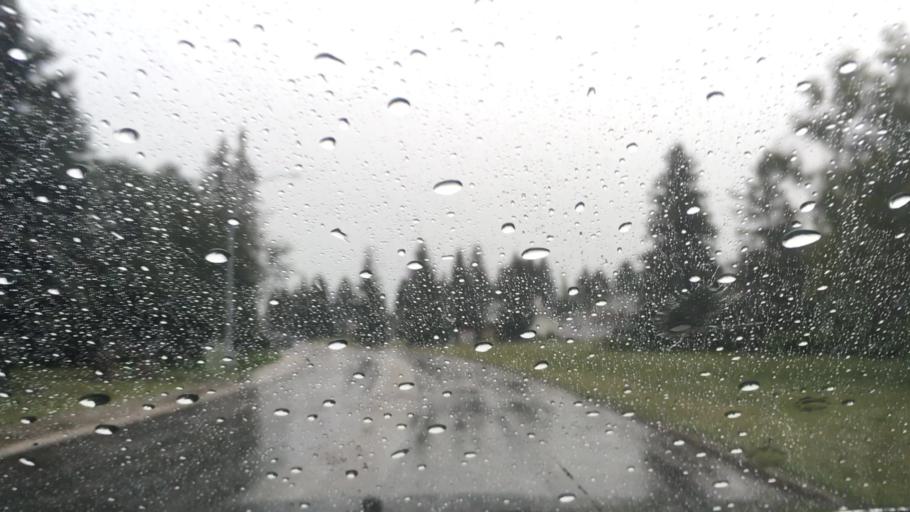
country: CA
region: Alberta
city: Edmonton
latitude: 53.4630
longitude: -113.5434
